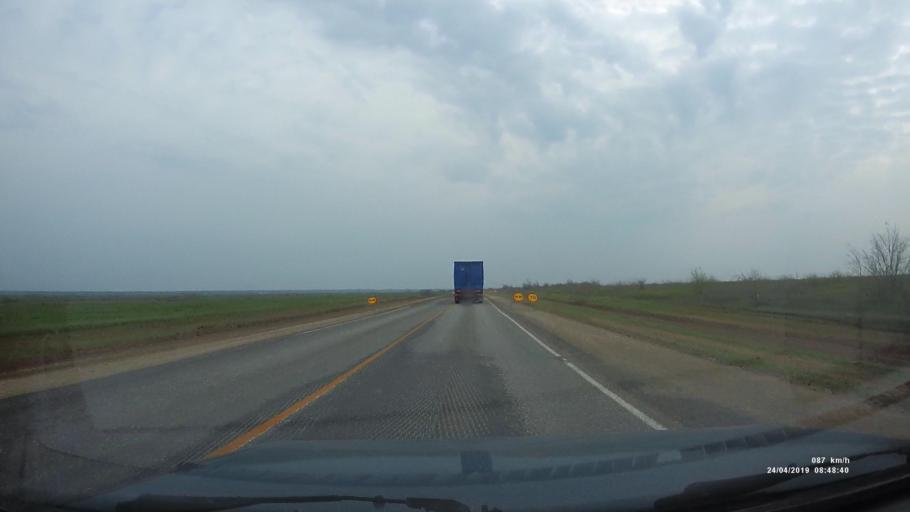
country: RU
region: Kalmykiya
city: Arshan'
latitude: 46.2524
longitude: 44.1126
